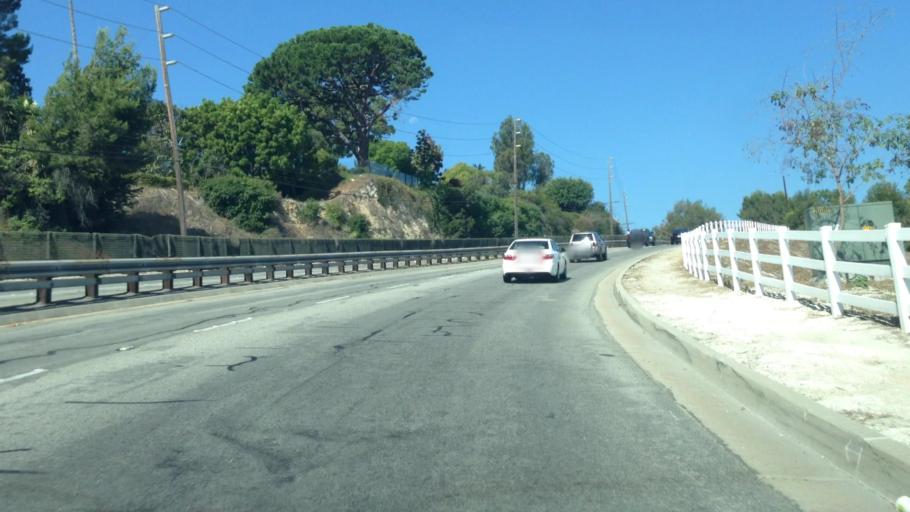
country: US
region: California
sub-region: Los Angeles County
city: Rolling Hills
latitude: 33.7678
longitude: -118.3674
